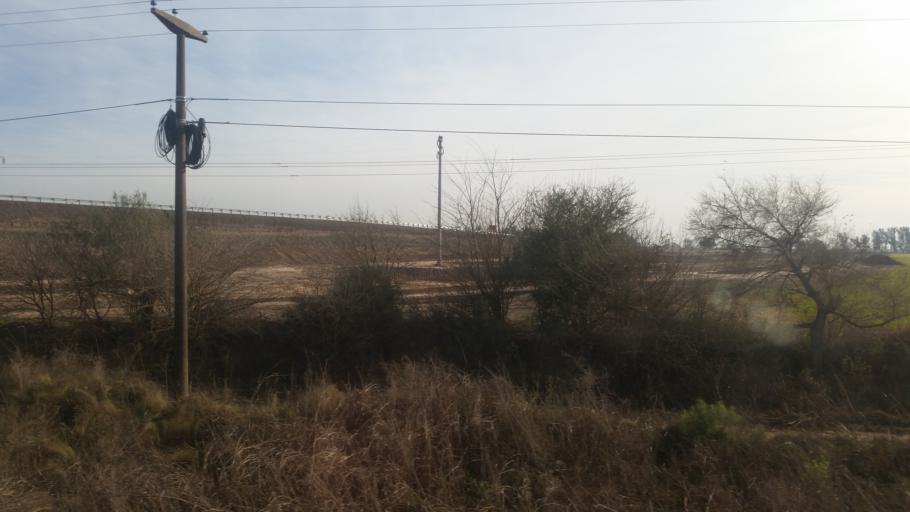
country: AR
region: Cordoba
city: Bell Ville
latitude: -32.6151
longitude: -62.7152
